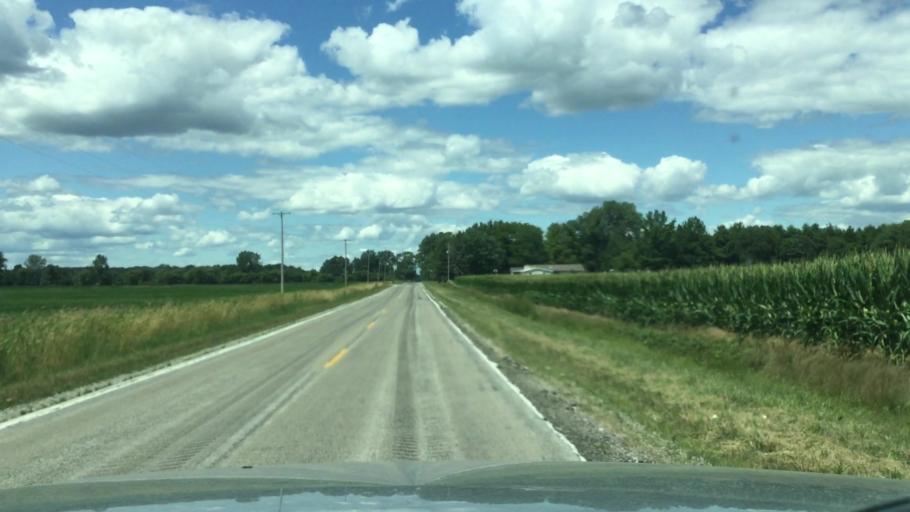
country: US
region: Michigan
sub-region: Saginaw County
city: Saint Charles
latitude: 43.3397
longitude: -84.1898
